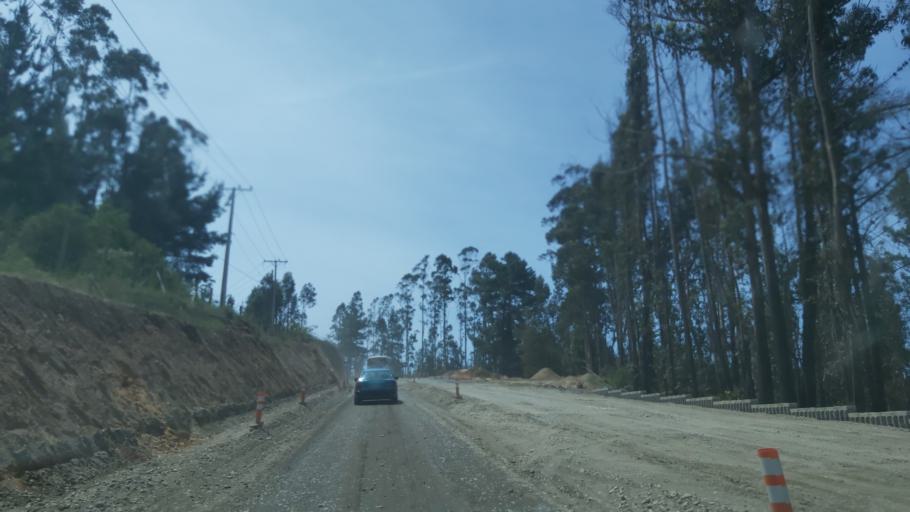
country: CL
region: Maule
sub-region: Provincia de Talca
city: Constitucion
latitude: -35.3861
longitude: -72.4198
